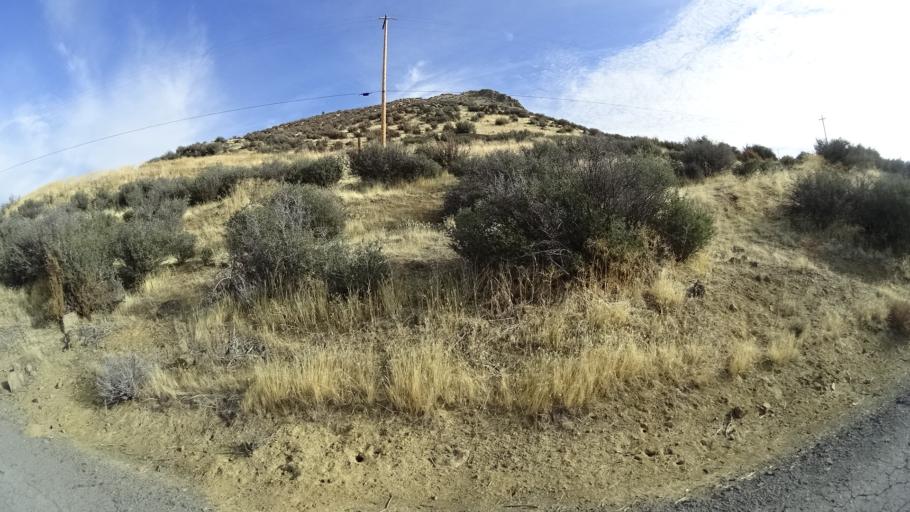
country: US
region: California
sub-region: Siskiyou County
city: Montague
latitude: 41.7113
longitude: -122.5212
